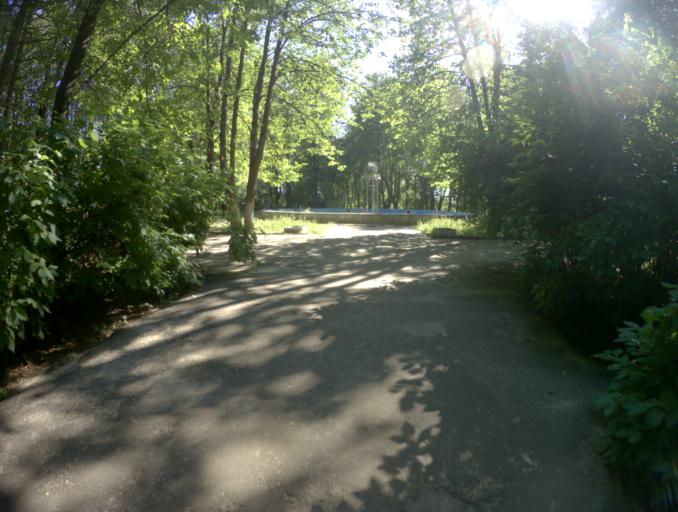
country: RU
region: Nizjnij Novgorod
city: Pavlovo
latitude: 55.9755
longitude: 43.0864
